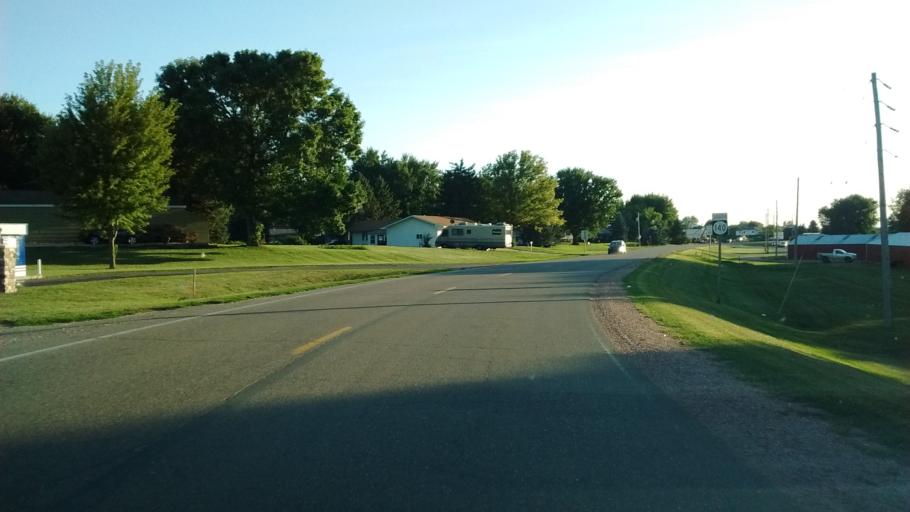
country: US
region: Iowa
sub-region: Plymouth County
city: Kingsley
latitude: 42.5847
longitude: -95.9677
